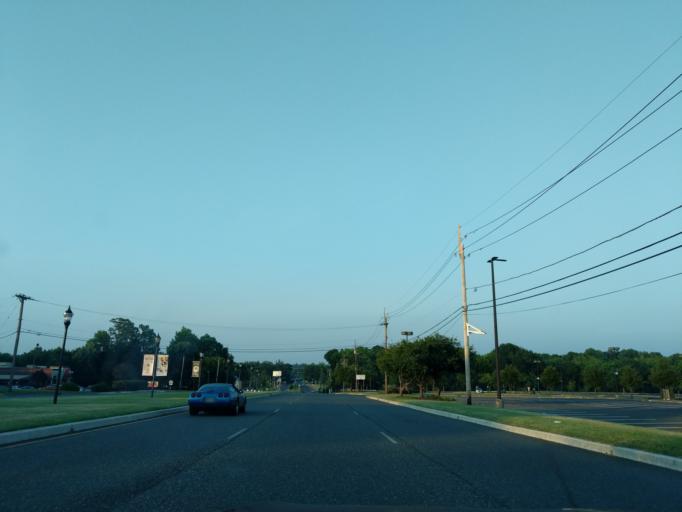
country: US
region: New Jersey
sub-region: Camden County
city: Glendora
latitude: 39.8340
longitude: -75.0985
